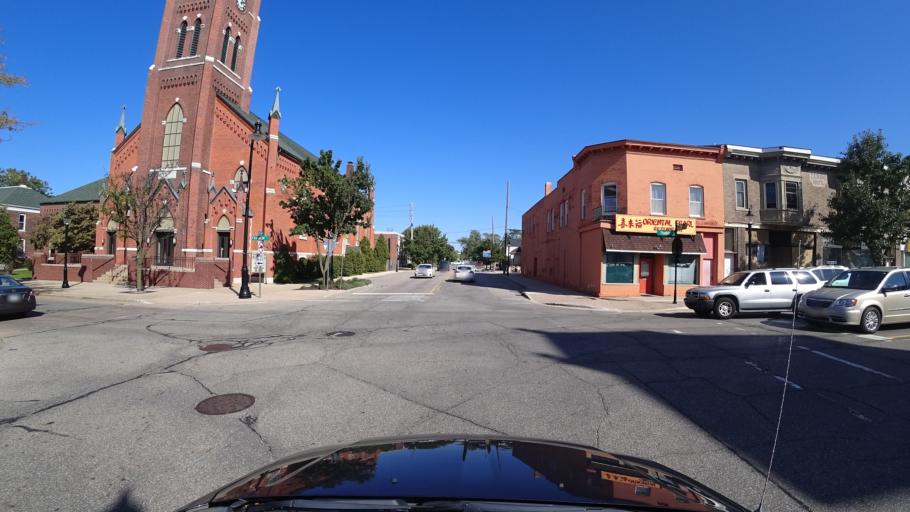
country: US
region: Indiana
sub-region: LaPorte County
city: Michigan City
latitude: 41.7128
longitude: -86.8997
